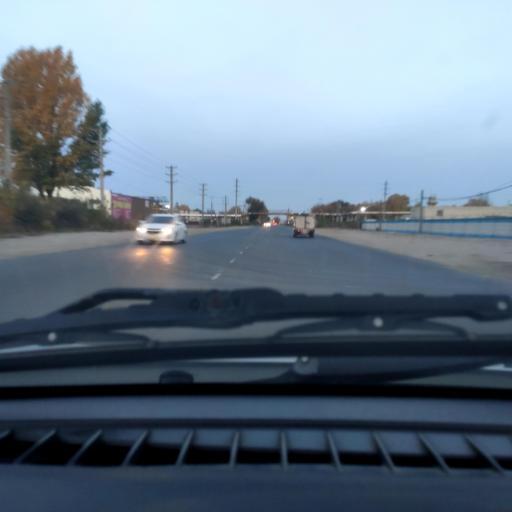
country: RU
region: Samara
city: Tol'yatti
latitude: 53.5303
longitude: 49.4657
